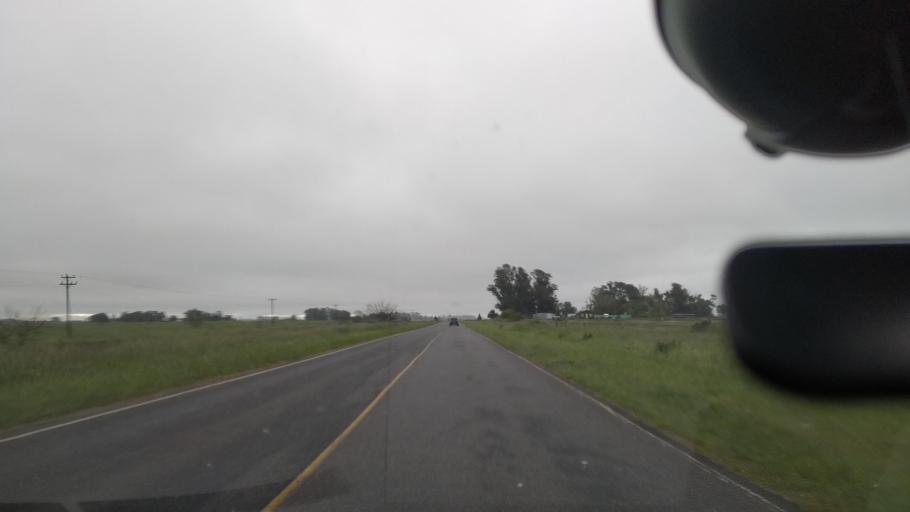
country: AR
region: Buenos Aires
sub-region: Partido de Magdalena
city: Magdalena
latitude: -35.2239
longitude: -57.7321
